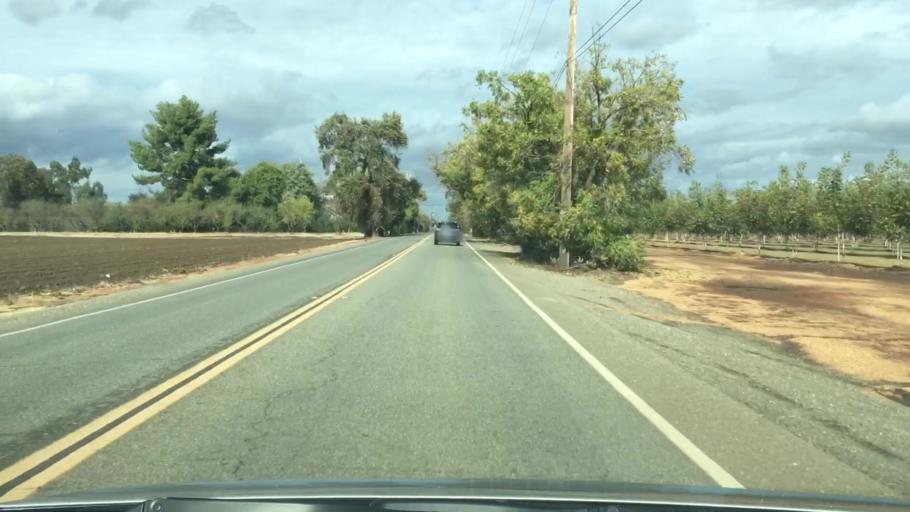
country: US
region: California
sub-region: Yolo County
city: Davis
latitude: 38.5555
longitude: -121.8032
